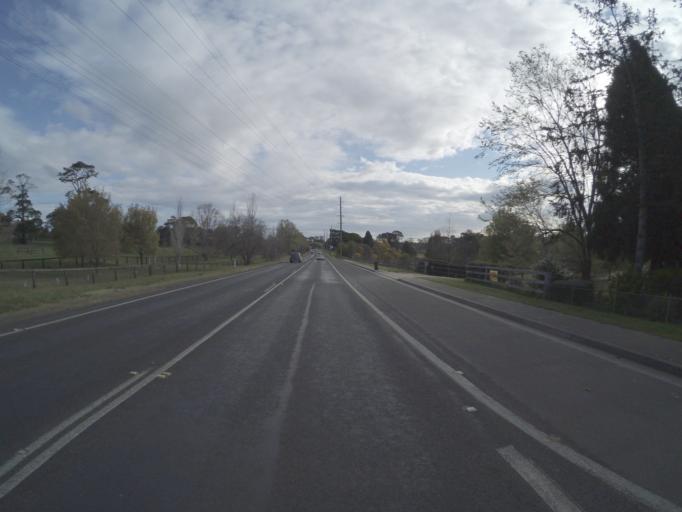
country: AU
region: New South Wales
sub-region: Wingecarribee
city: Moss Vale
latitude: -34.5687
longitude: 150.3204
